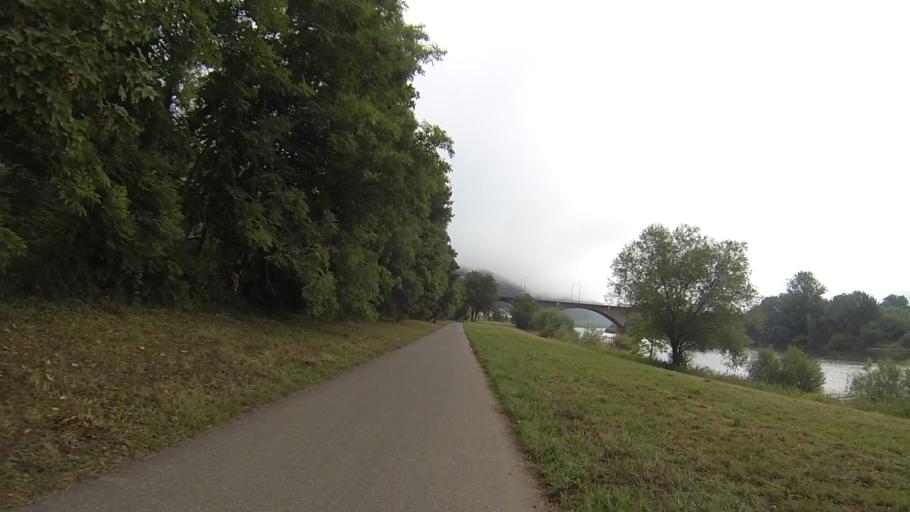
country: DE
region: Rheinland-Pfalz
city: Trier
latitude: 49.7633
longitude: 6.6296
